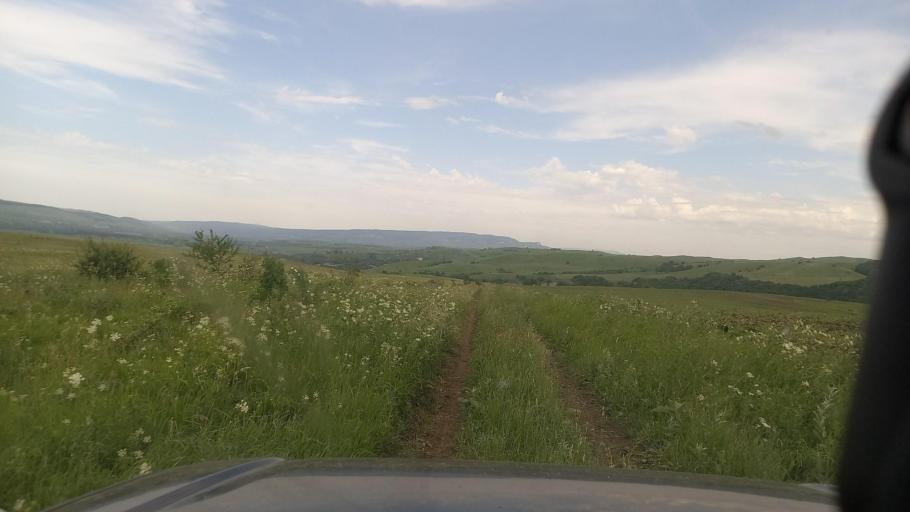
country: RU
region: Krasnodarskiy
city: Peredovaya
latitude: 44.0785
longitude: 41.3365
